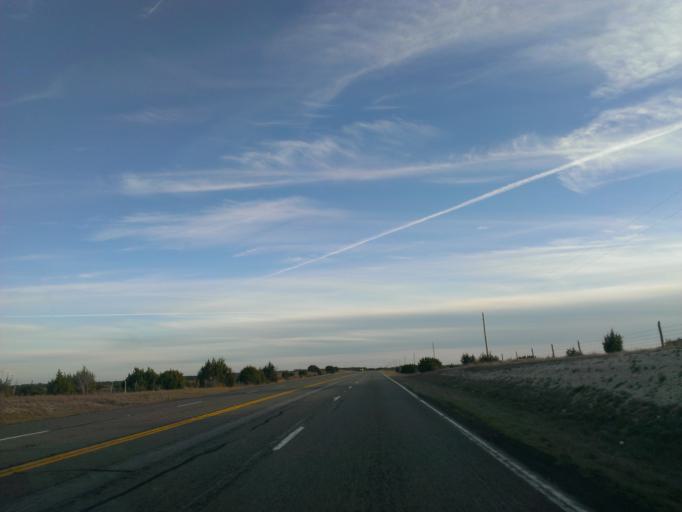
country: US
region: Texas
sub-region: Lampasas County
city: Kempner
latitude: 30.9099
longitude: -97.9738
